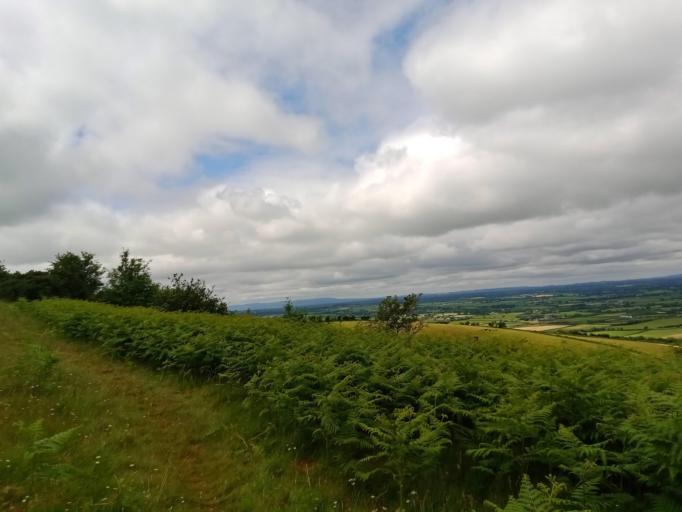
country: IE
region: Leinster
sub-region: Laois
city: Rathdowney
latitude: 52.8001
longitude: -7.4727
